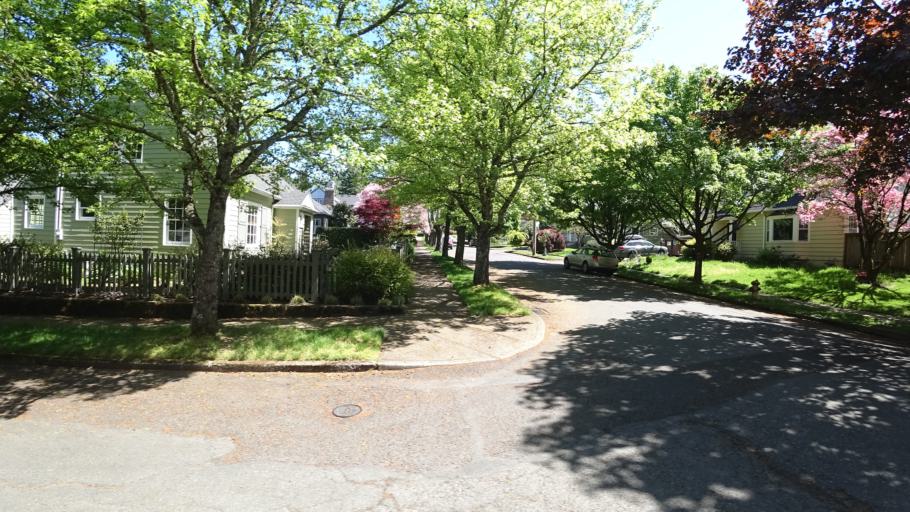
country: US
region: Oregon
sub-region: Clackamas County
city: Milwaukie
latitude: 45.4740
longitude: -122.6244
